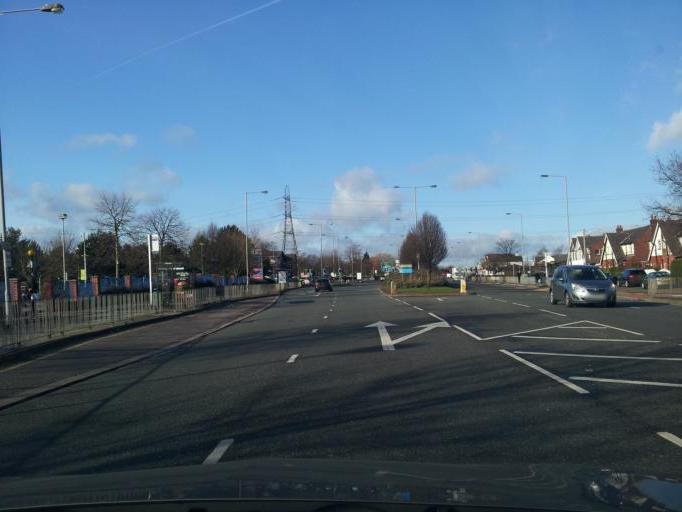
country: GB
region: England
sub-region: Borough of Bury
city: Prestwich
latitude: 53.5354
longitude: -2.2871
